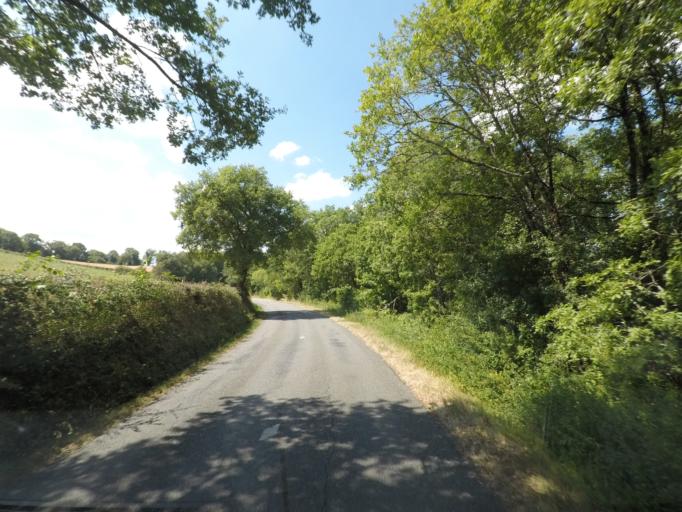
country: FR
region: Midi-Pyrenees
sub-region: Departement du Lot
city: Cahors
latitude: 44.5733
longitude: 1.5795
